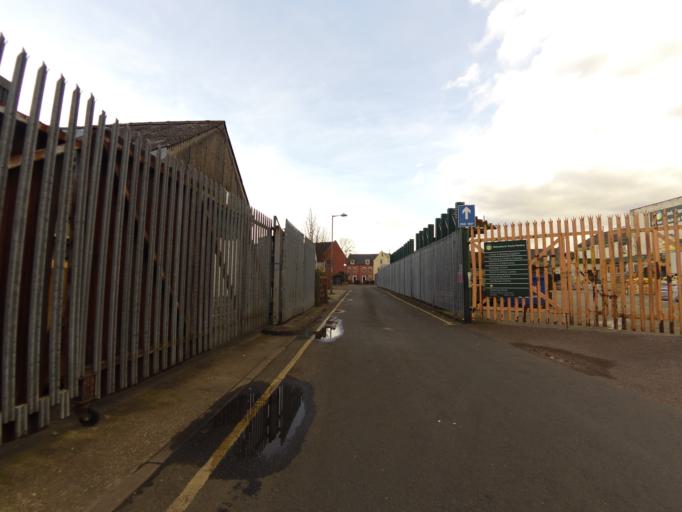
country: GB
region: England
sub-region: Suffolk
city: Ipswich
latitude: 52.0588
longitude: 1.1389
